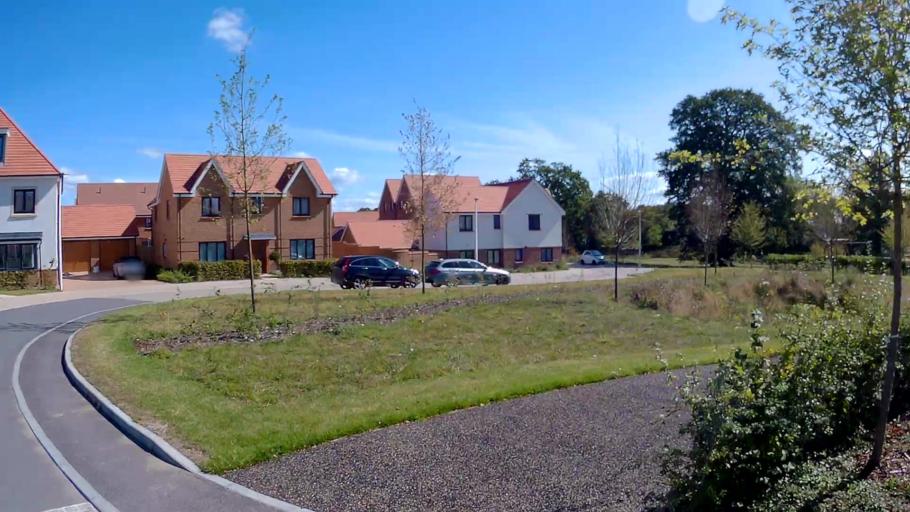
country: GB
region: England
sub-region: West Berkshire
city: Arborfield
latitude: 51.3799
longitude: -0.9027
